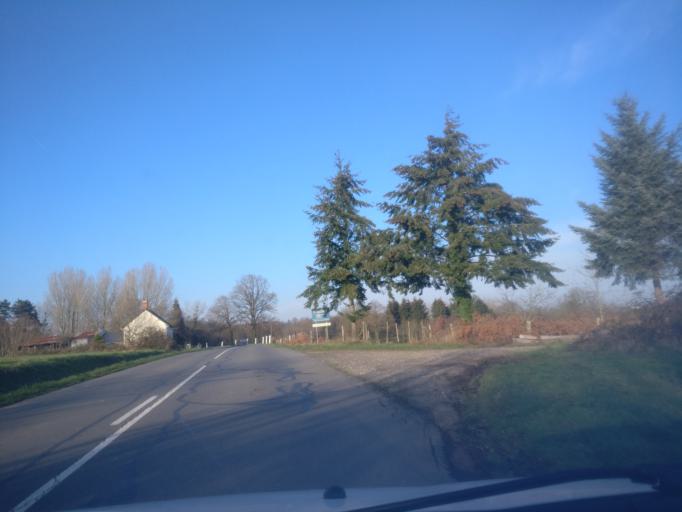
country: FR
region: Brittany
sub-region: Departement d'Ille-et-Vilaine
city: Livre-sur-Changeon
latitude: 48.2133
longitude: -1.3374
